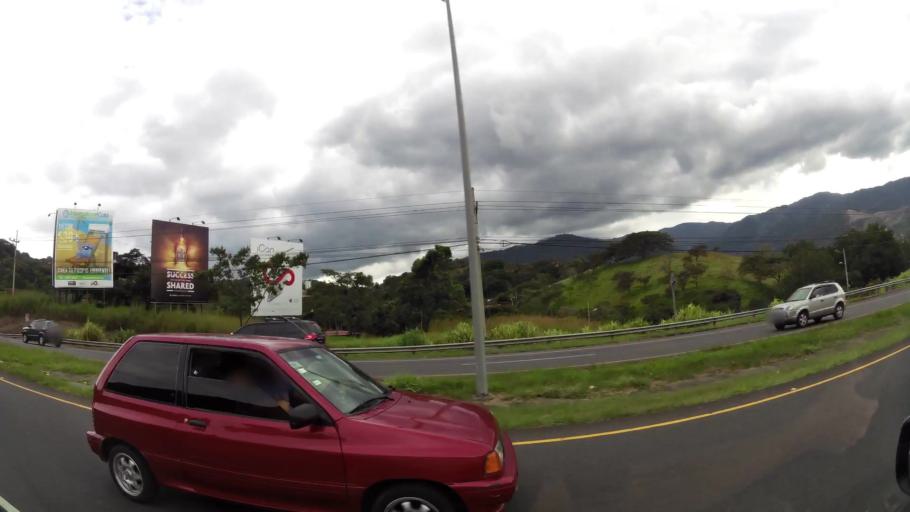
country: CR
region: San Jose
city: Santa Ana
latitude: 9.9479
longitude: -84.1783
